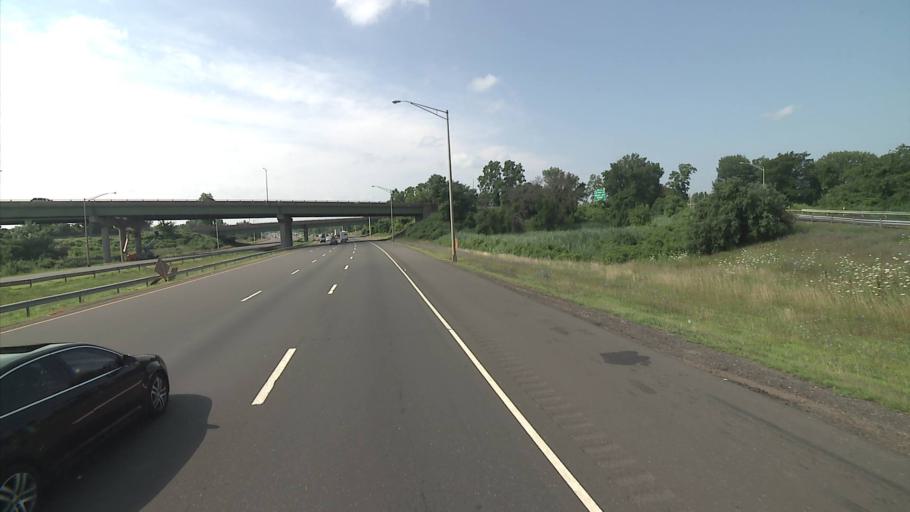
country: US
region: Connecticut
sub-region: New Haven County
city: North Haven
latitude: 41.3779
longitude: -72.8688
